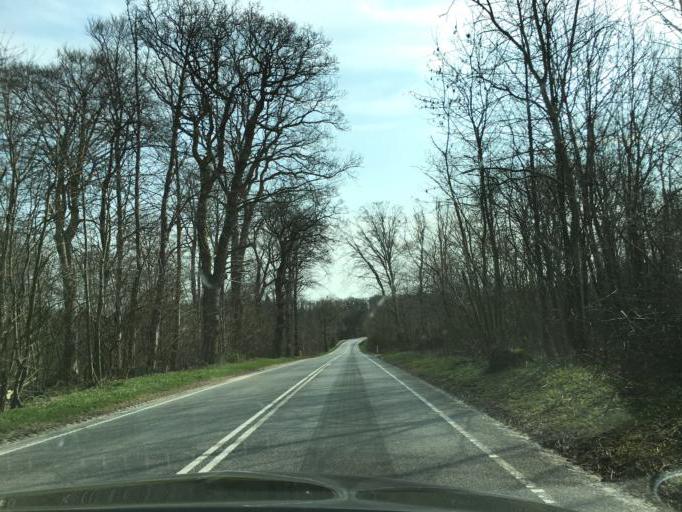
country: DK
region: South Denmark
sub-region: Vejen Kommune
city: Brorup
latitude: 55.4946
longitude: 9.0636
